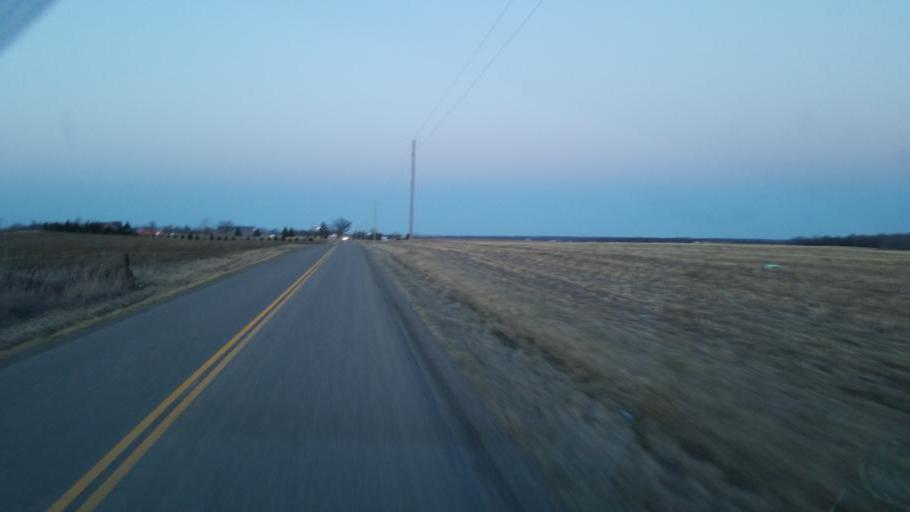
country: US
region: Ohio
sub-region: Champaign County
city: North Lewisburg
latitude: 40.2391
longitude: -83.6125
